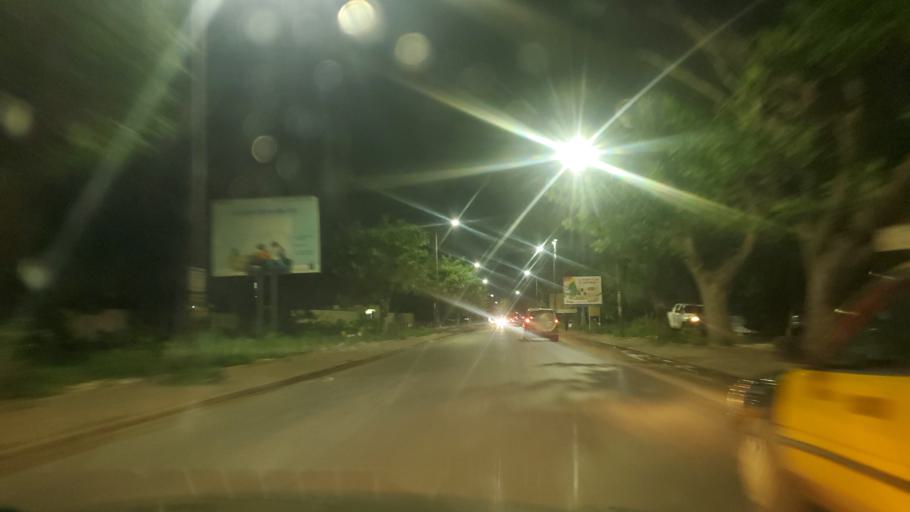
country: SN
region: Dakar
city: Mermoz Boabab
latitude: 14.7004
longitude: -17.4661
